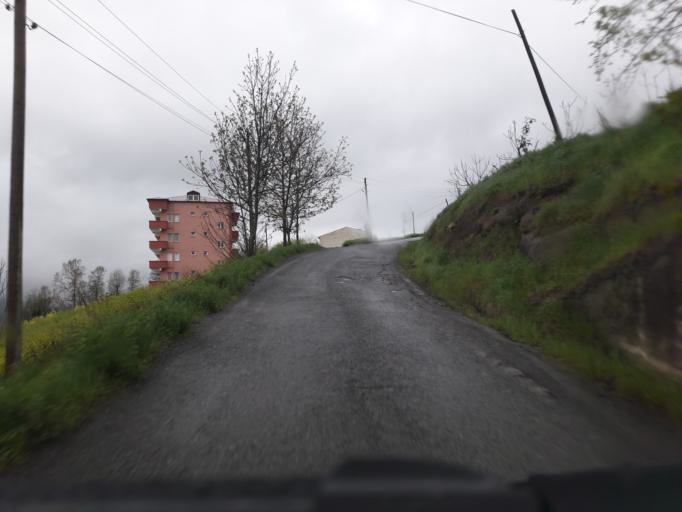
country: TR
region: Trabzon
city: Duzkoy
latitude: 40.9274
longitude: 39.4771
